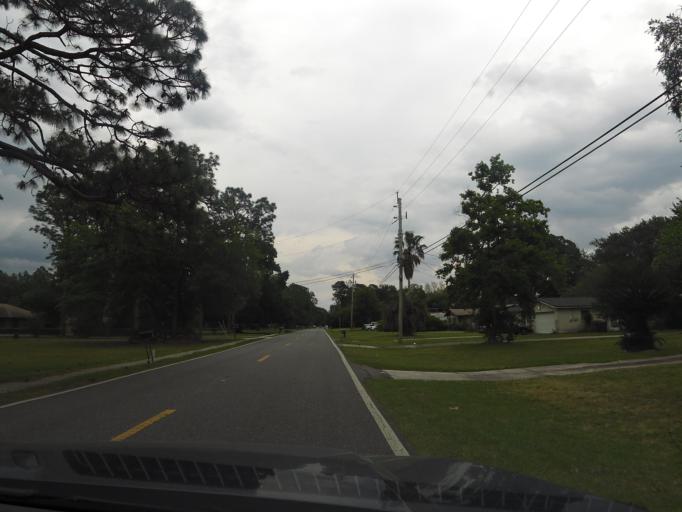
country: US
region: Florida
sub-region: Duval County
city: Jacksonville
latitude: 30.3295
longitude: -81.7942
